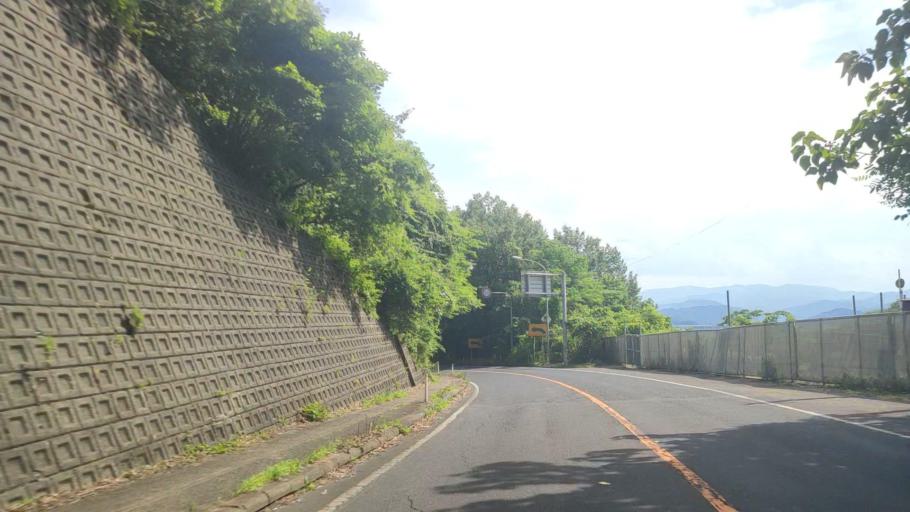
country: JP
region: Tottori
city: Tottori
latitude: 35.5306
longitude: 134.2292
